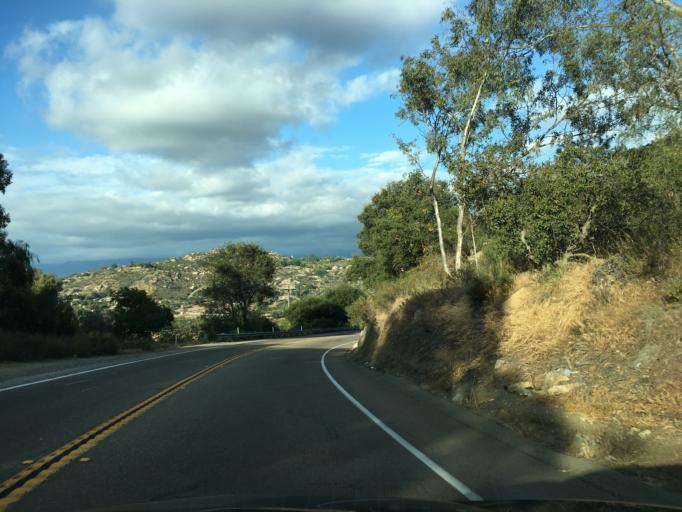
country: US
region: California
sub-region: San Diego County
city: Hidden Meadows
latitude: 33.2571
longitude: -117.0763
